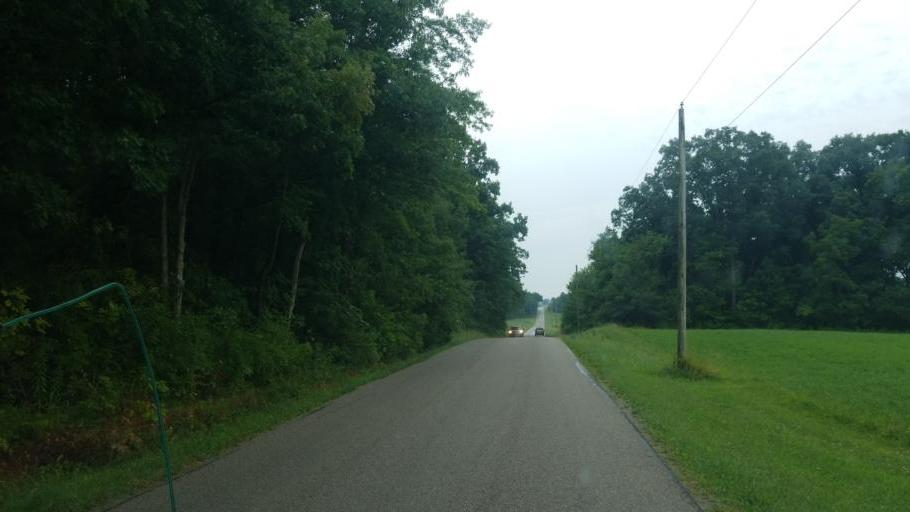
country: US
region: Ohio
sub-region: Williams County
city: Edgerton
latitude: 41.4356
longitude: -84.6703
